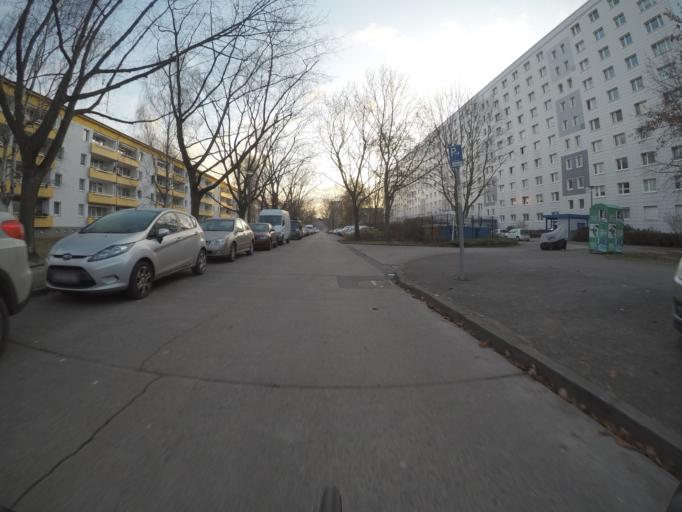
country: DE
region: Berlin
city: Friedrichsfelde
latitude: 52.4960
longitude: 13.5031
